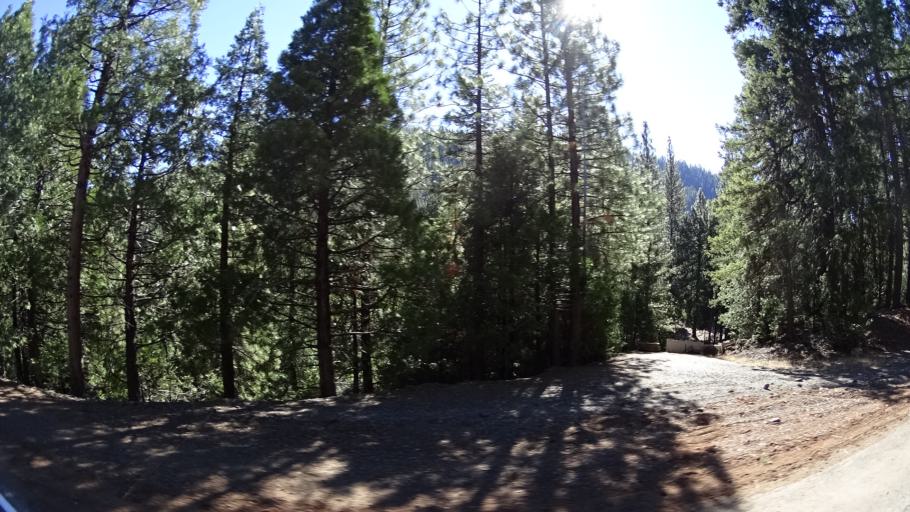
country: US
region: California
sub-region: Siskiyou County
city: Weed
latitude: 41.2687
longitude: -122.8814
